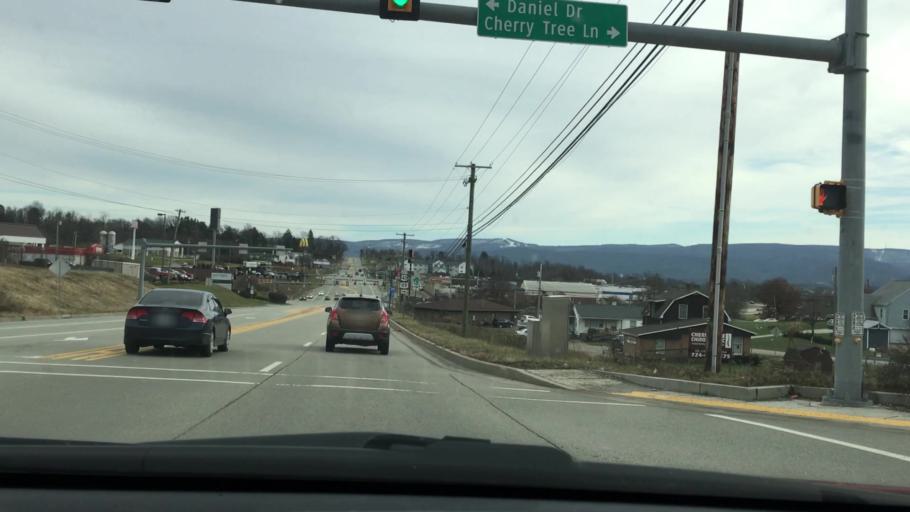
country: US
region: Pennsylvania
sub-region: Fayette County
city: South Uniontown
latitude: 39.9022
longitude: -79.7579
